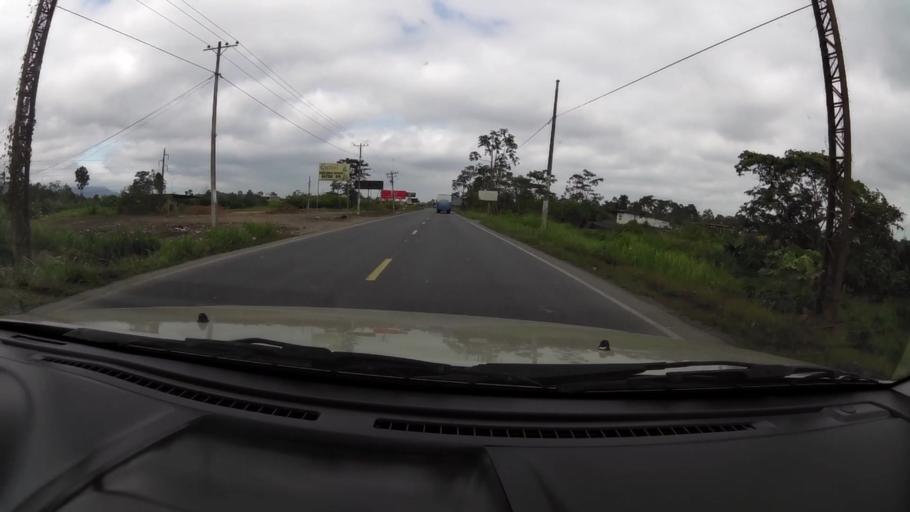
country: EC
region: Guayas
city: Naranjal
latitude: -2.6852
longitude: -79.6296
